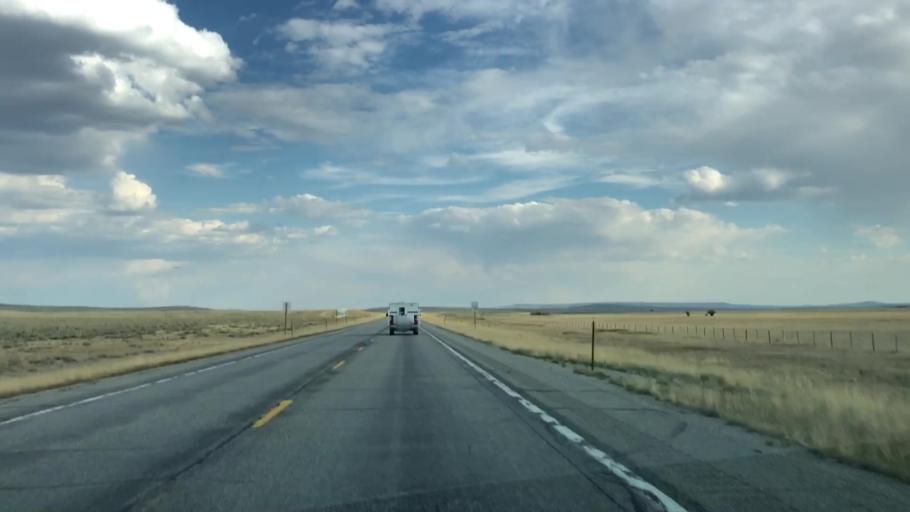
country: US
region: Wyoming
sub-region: Sublette County
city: Pinedale
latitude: 43.0410
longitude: -110.1400
